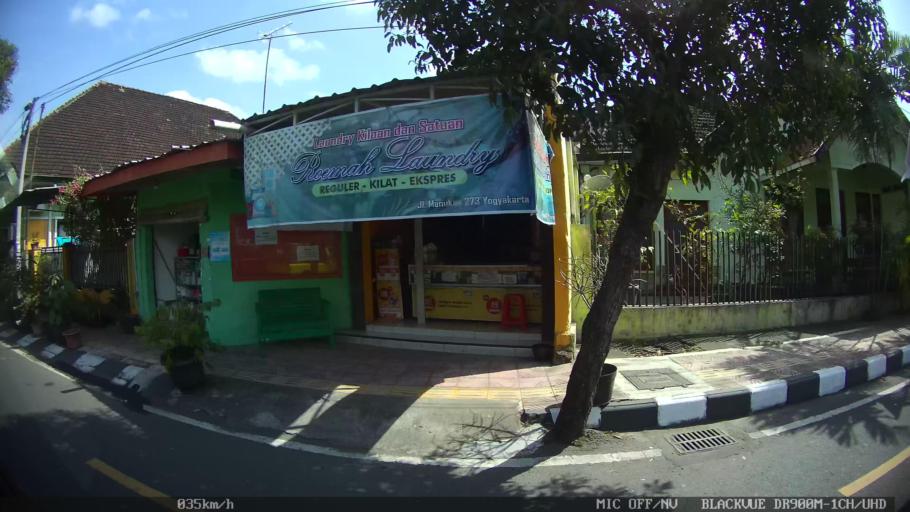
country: ID
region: Daerah Istimewa Yogyakarta
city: Kasihan
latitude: -7.8242
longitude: 110.3713
